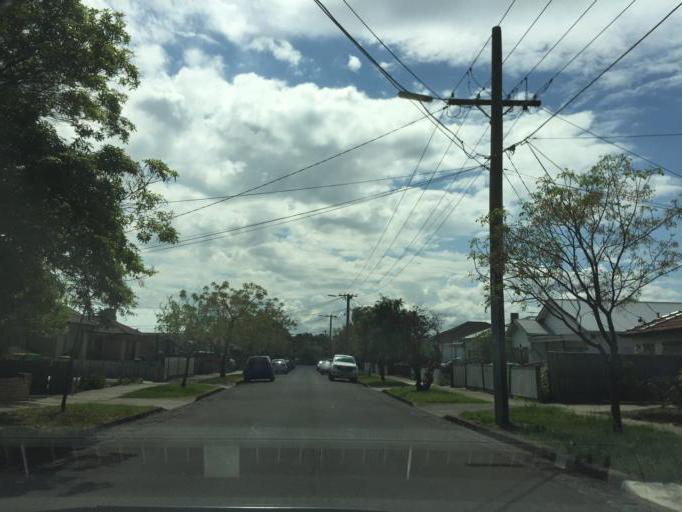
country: AU
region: Victoria
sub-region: Maribyrnong
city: West Footscray
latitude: -37.7919
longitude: 144.8807
